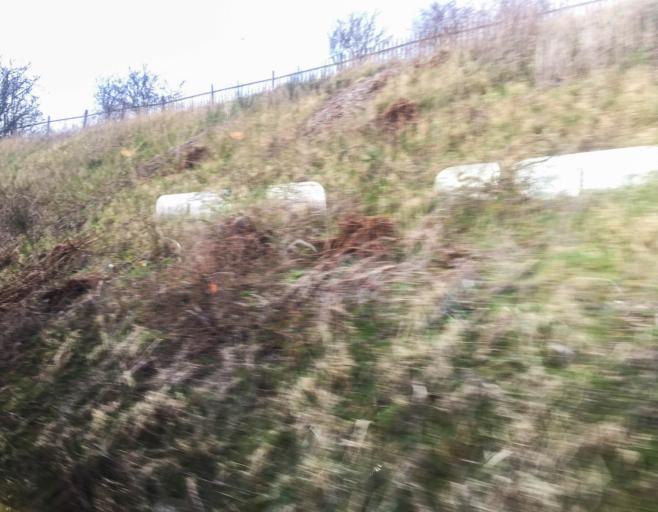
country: GB
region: Scotland
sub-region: North Lanarkshire
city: Wishaw
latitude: 55.7628
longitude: -3.9096
